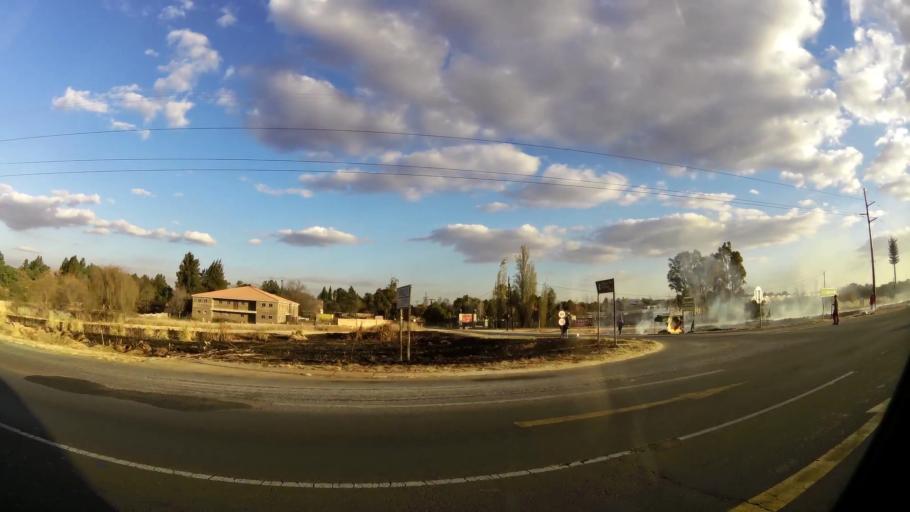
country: ZA
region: Gauteng
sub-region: City of Johannesburg Metropolitan Municipality
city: Midrand
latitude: -25.9476
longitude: 28.1656
